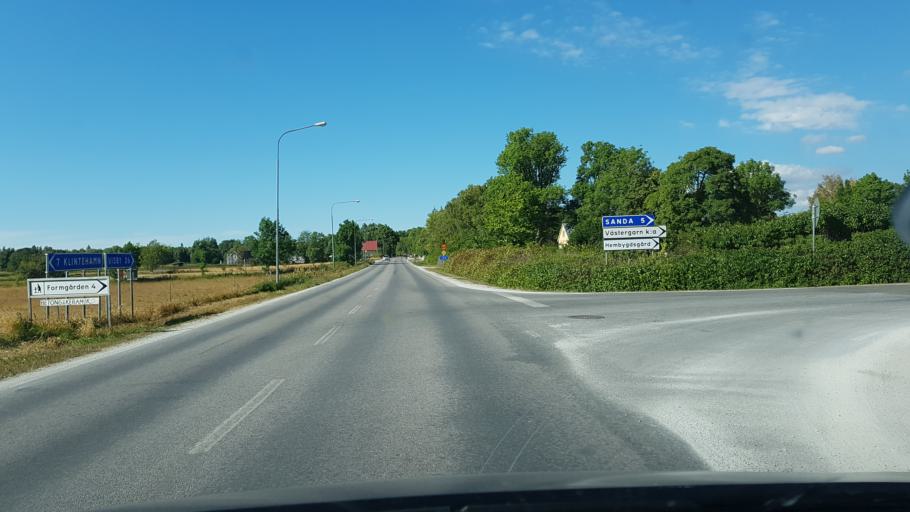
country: SE
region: Gotland
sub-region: Gotland
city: Klintehamn
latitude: 57.4402
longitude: 18.1451
